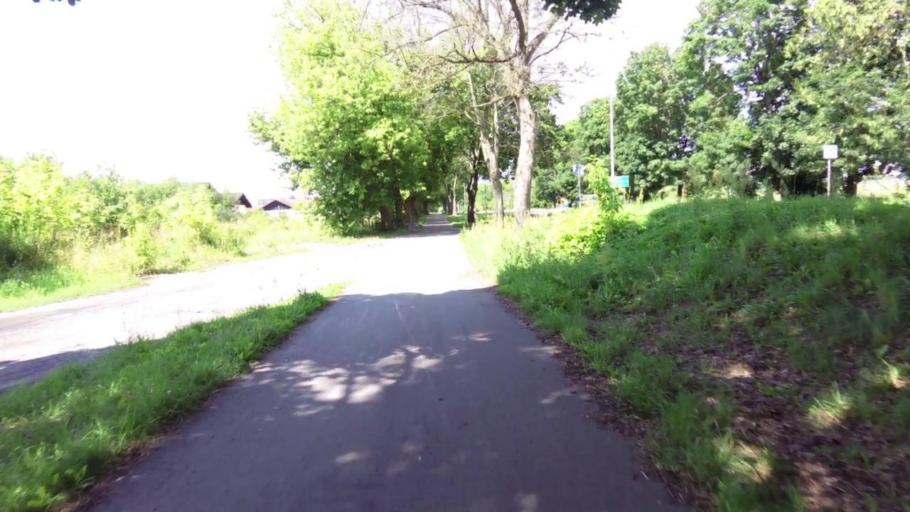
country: PL
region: West Pomeranian Voivodeship
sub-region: Powiat stargardzki
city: Kobylanka
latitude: 53.3471
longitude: 14.8505
